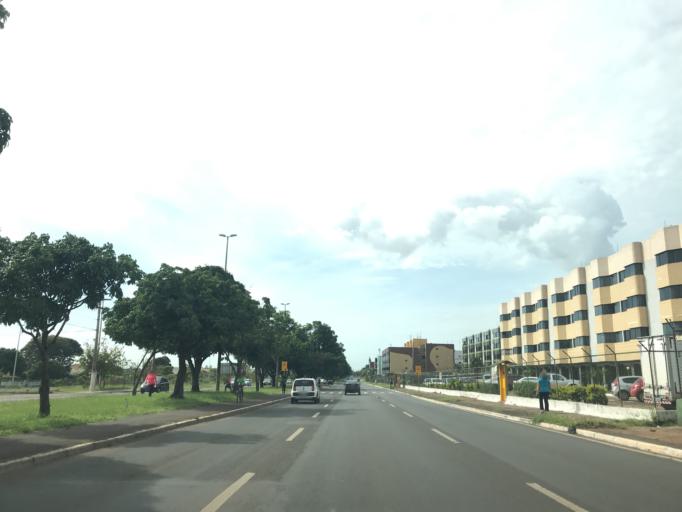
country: BR
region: Federal District
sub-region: Brasilia
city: Brasilia
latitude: -15.8205
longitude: -48.0867
